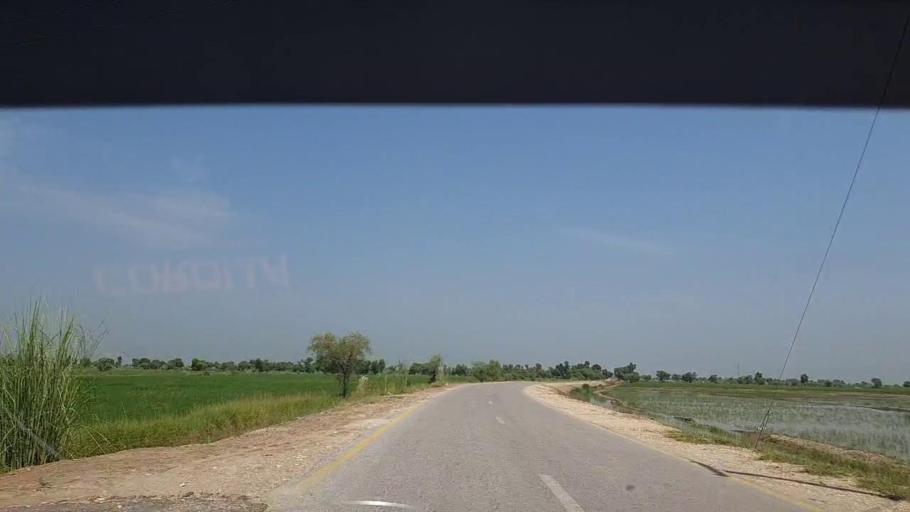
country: PK
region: Sindh
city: Rustam jo Goth
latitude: 28.1060
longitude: 68.8046
